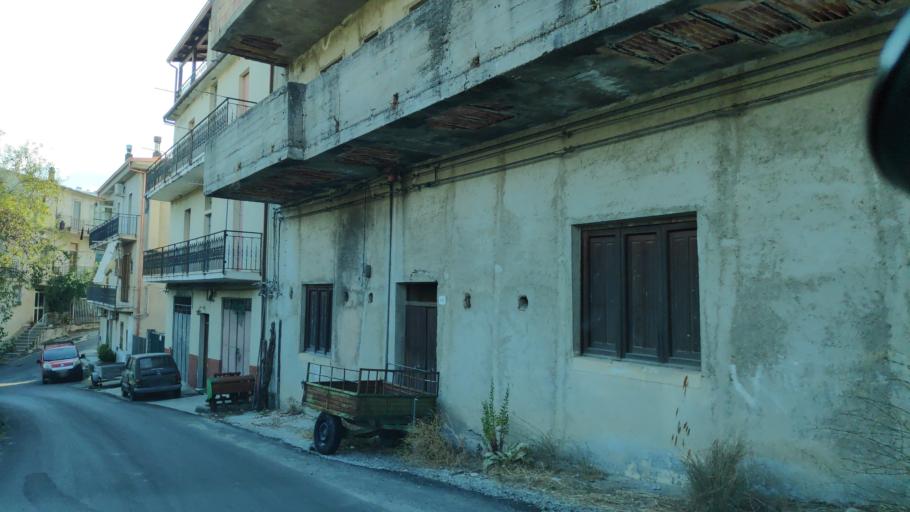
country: IT
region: Calabria
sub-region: Provincia di Catanzaro
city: Guardavalle
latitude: 38.5079
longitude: 16.5010
